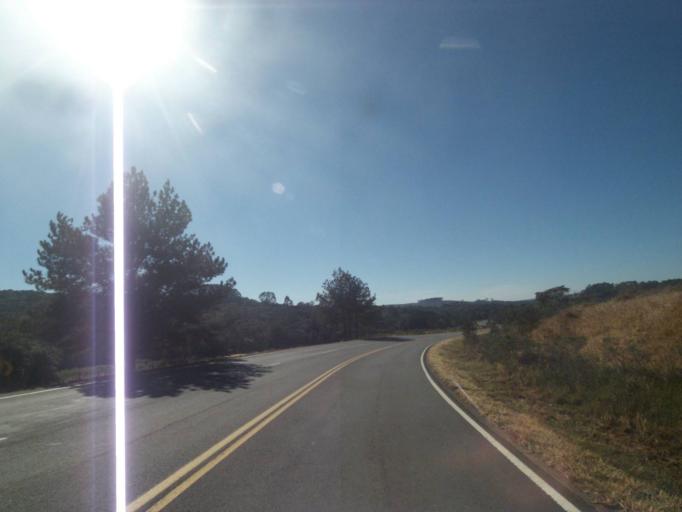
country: BR
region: Parana
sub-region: Tibagi
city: Tibagi
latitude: -24.4694
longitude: -50.5024
